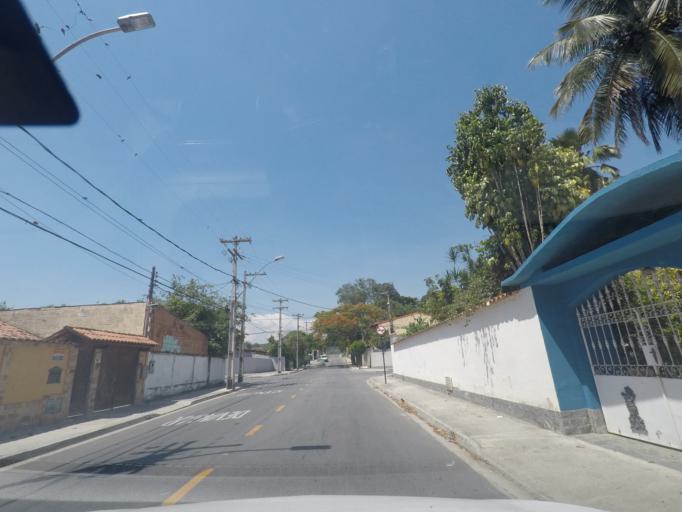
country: BR
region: Rio de Janeiro
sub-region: Niteroi
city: Niteroi
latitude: -22.9467
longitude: -43.0294
